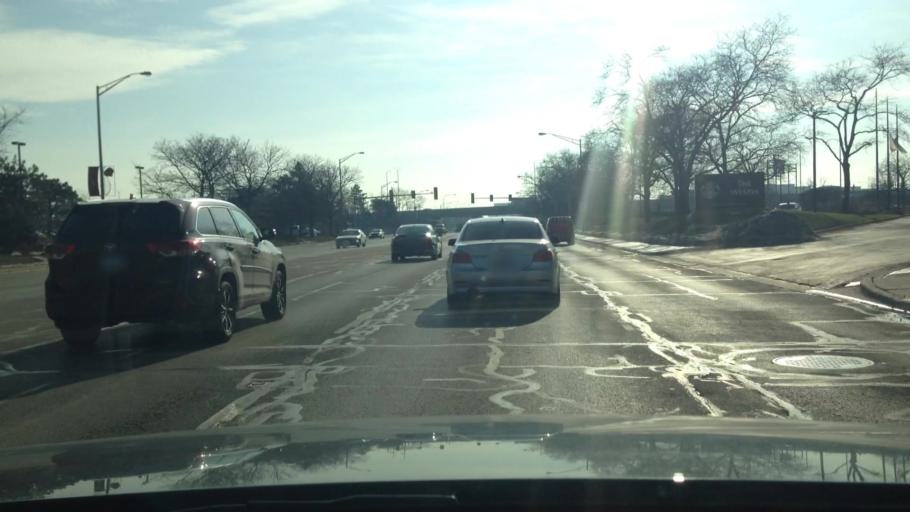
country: US
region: Illinois
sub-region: Cook County
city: Rosemont
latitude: 41.9895
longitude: -87.8602
